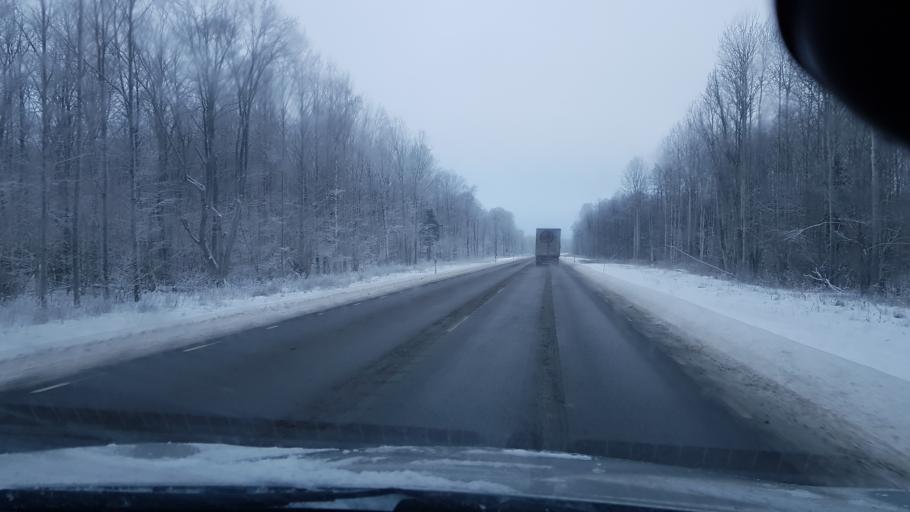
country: EE
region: Harju
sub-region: Paldiski linn
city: Paldiski
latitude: 59.3398
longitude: 24.1325
